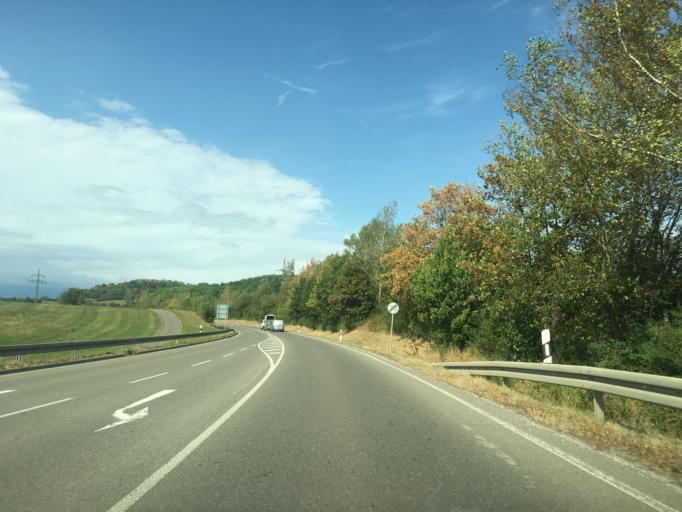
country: DE
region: Baden-Wuerttemberg
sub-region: Tuebingen Region
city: Gomaringen
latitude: 48.4480
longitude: 9.1544
